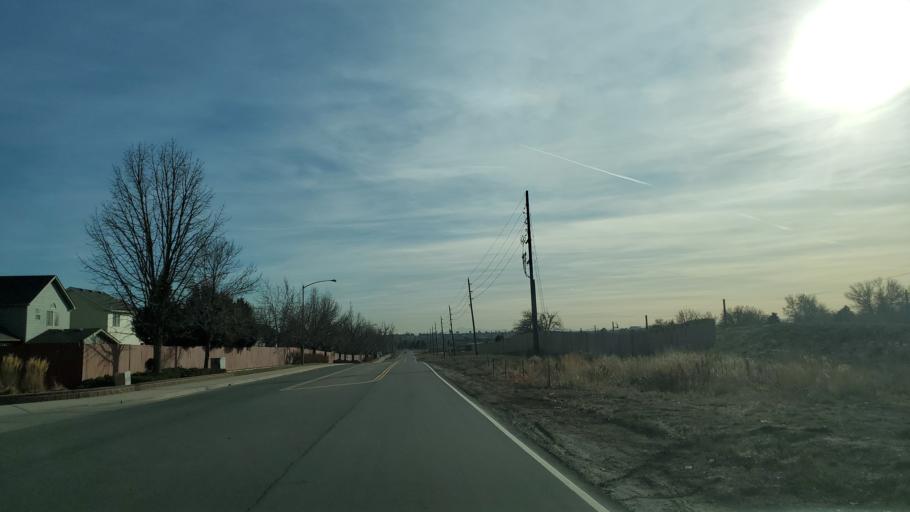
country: US
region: Colorado
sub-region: Adams County
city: Northglenn
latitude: 39.9072
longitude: -104.9589
